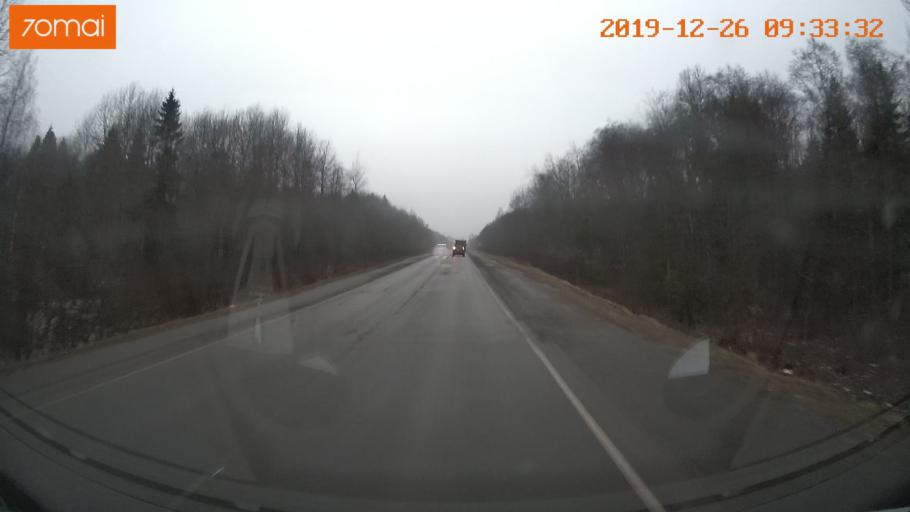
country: RU
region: Vologda
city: Vologda
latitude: 59.0910
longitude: 40.0991
